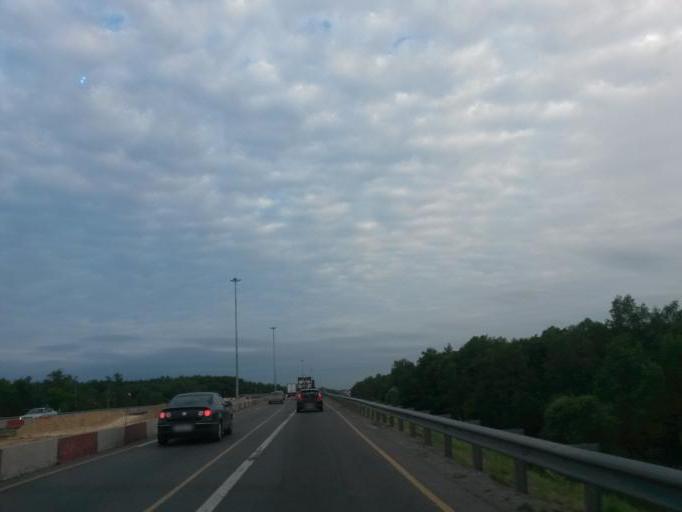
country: RU
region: Moskovskaya
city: Lyubuchany
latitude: 55.2101
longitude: 37.5348
